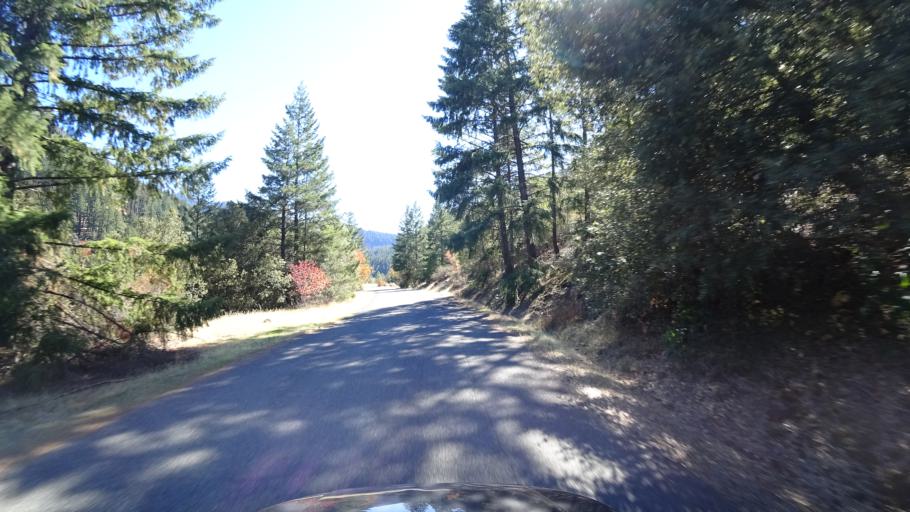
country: US
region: California
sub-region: Humboldt County
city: Willow Creek
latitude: 41.3091
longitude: -123.3754
